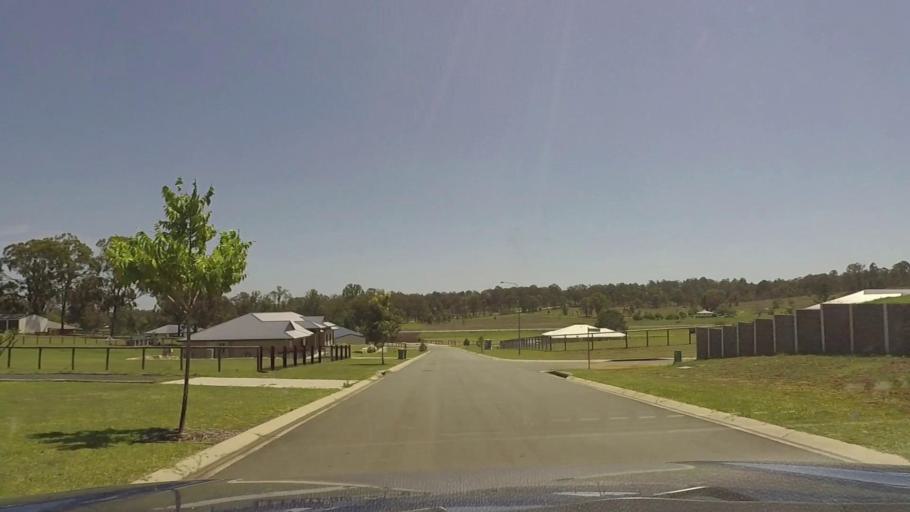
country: AU
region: Queensland
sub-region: Logan
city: Cedar Vale
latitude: -27.8886
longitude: 152.9830
